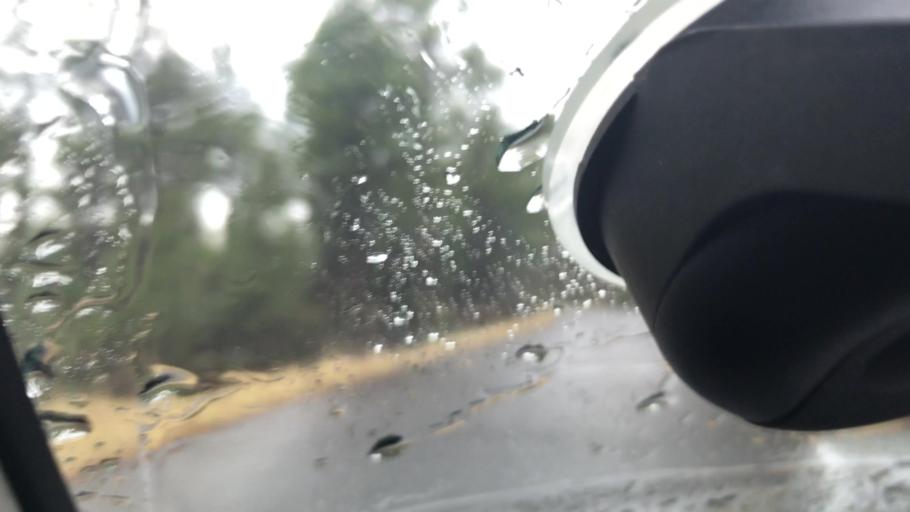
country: US
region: Arizona
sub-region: Yavapai County
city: Prescott
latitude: 34.5075
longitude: -112.3821
